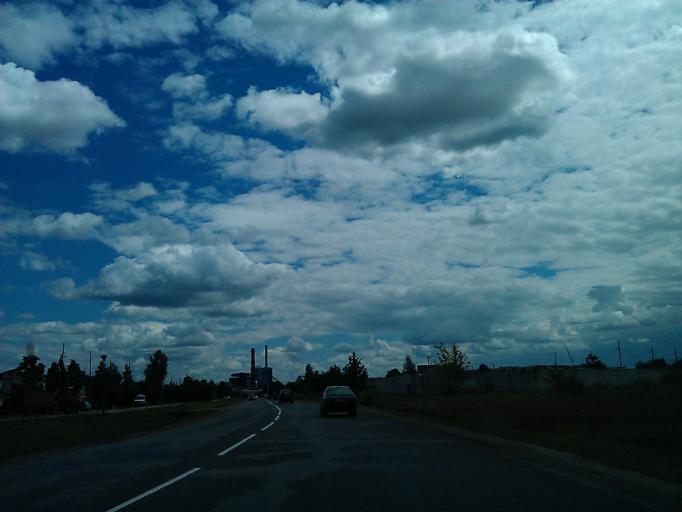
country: LV
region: Jelgava
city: Jelgava
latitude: 56.6401
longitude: 23.6979
